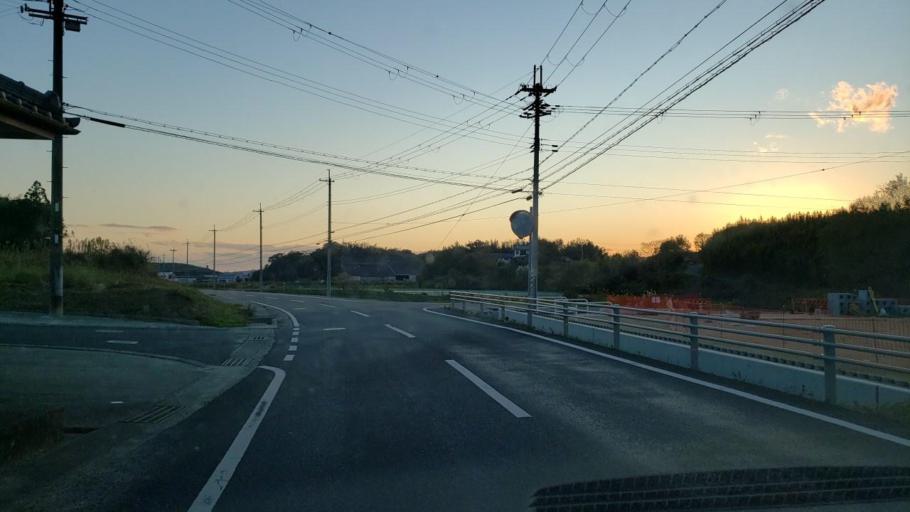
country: JP
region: Hyogo
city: Fukura
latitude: 34.3405
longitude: 134.7804
